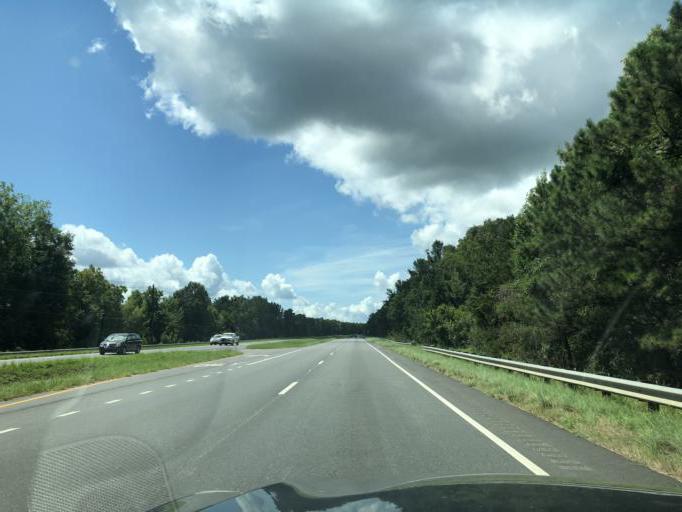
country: US
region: Alabama
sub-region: Barbour County
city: Eufaula
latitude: 31.9768
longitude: -85.1149
